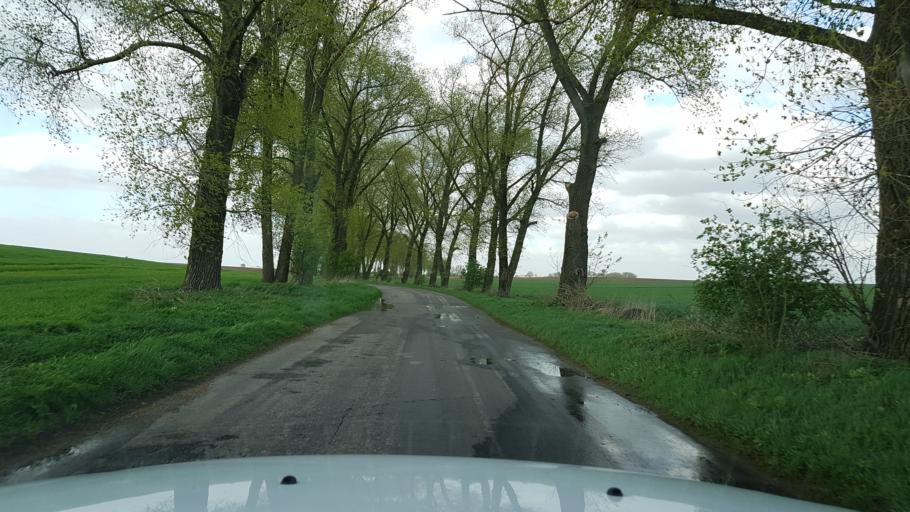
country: PL
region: West Pomeranian Voivodeship
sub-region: Powiat pyrzycki
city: Przelewice
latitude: 53.0305
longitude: 15.0800
